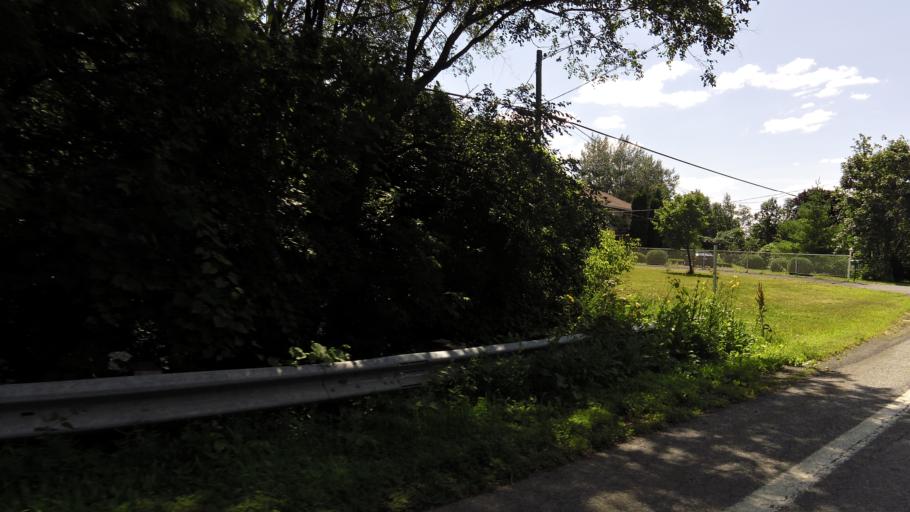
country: CA
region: Quebec
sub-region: Monteregie
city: Richelieu
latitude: 45.4011
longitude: -73.2602
